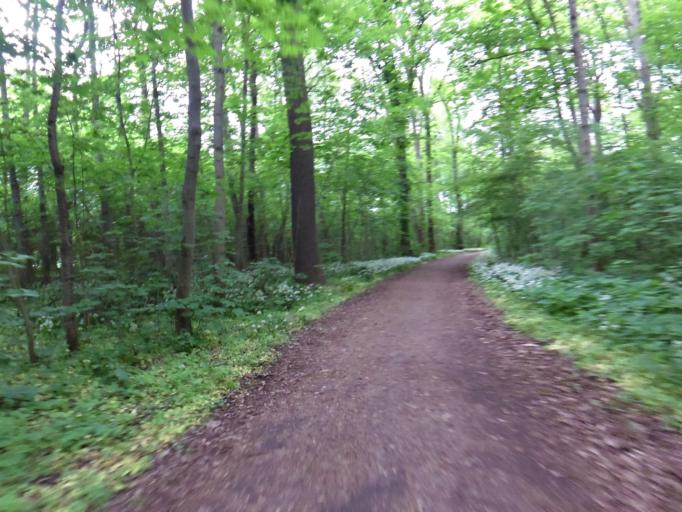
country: DE
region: Saxony
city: Leipzig
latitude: 51.3128
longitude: 12.3360
